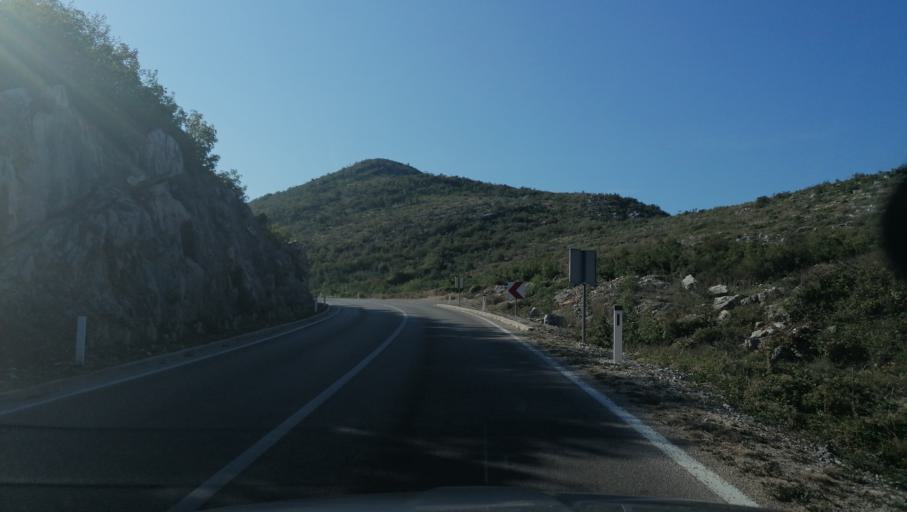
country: BA
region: Republika Srpska
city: Trebinje
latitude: 42.6523
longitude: 18.3653
